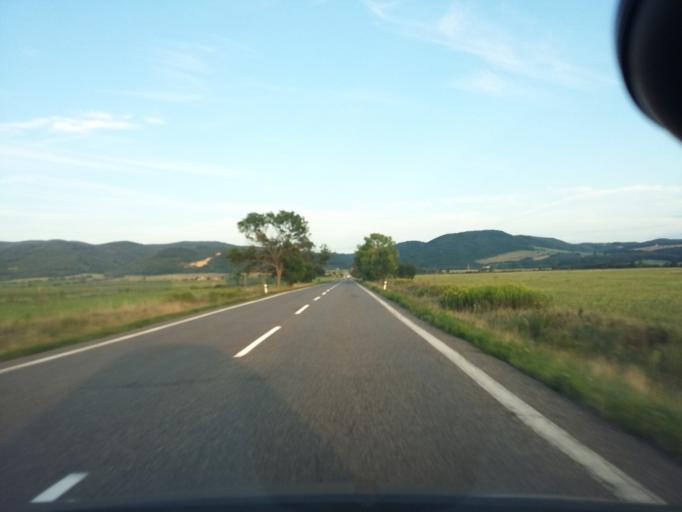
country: SK
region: Bratislavsky
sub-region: Okres Malacky
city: Malacky
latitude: 48.3849
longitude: 17.1081
